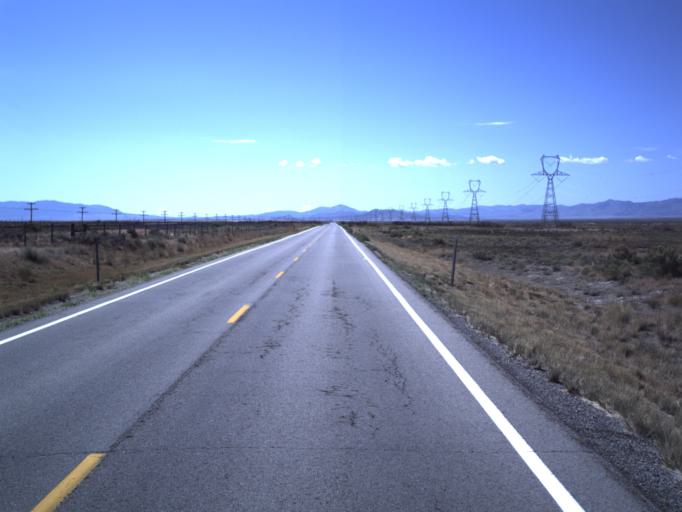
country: US
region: Utah
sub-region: Tooele County
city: Tooele
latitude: 40.3308
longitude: -112.4084
